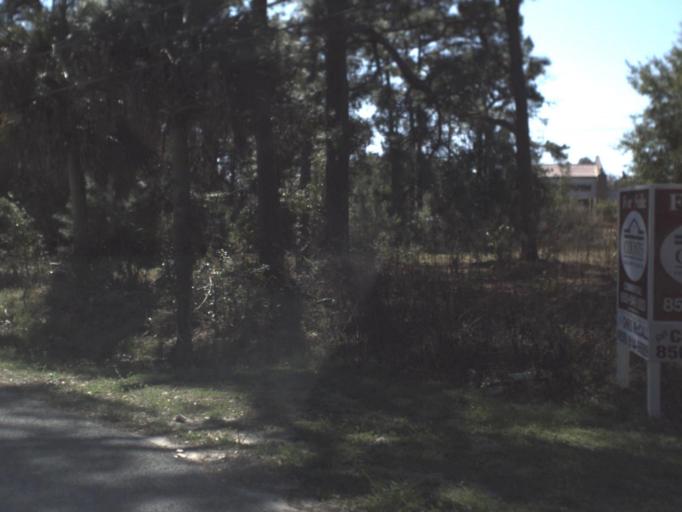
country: US
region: Florida
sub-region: Bay County
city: Panama City
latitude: 30.1833
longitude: -85.6687
